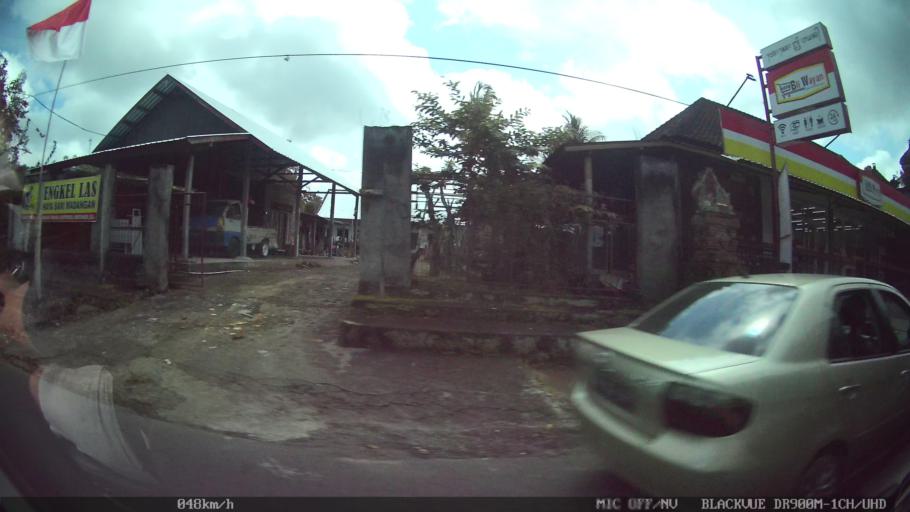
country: ID
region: Bali
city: Banjar Madangan Kaja
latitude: -8.4759
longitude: 115.3239
